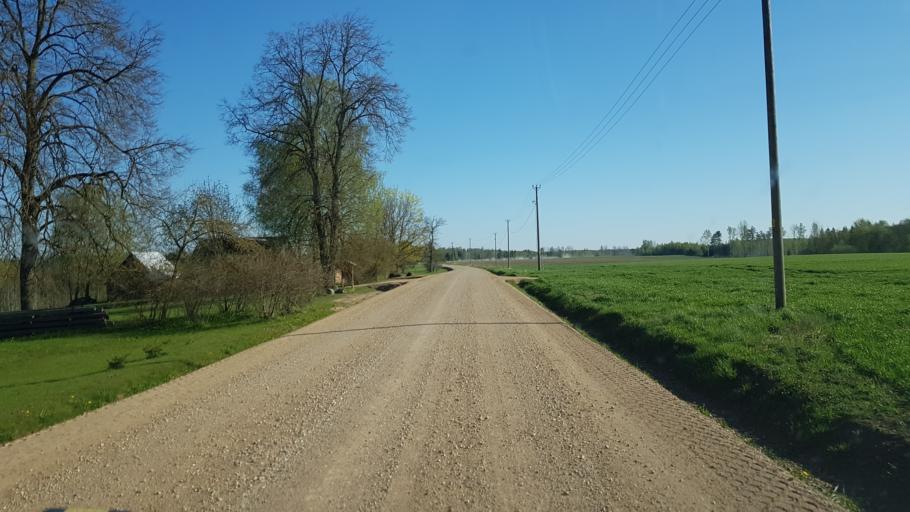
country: EE
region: Polvamaa
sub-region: Polva linn
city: Polva
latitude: 58.0970
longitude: 27.2219
